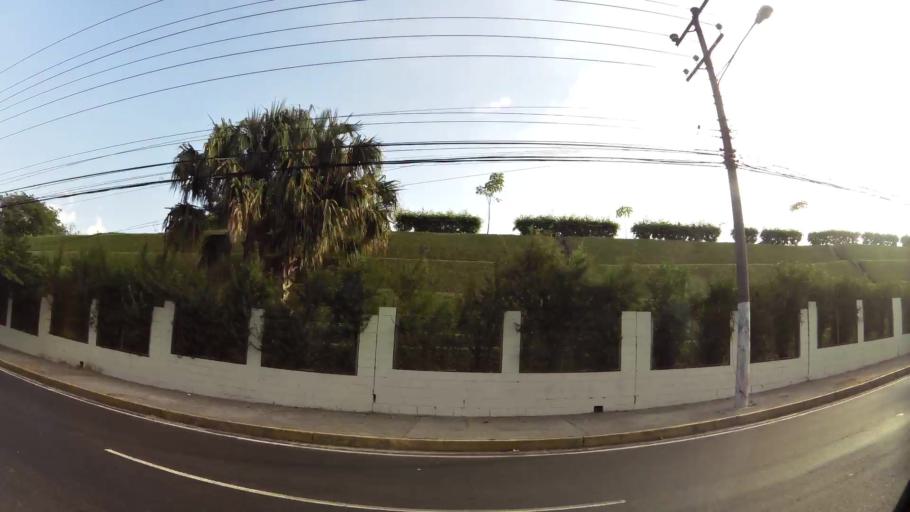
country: SV
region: San Salvador
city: San Salvador
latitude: 13.6918
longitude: -89.2095
